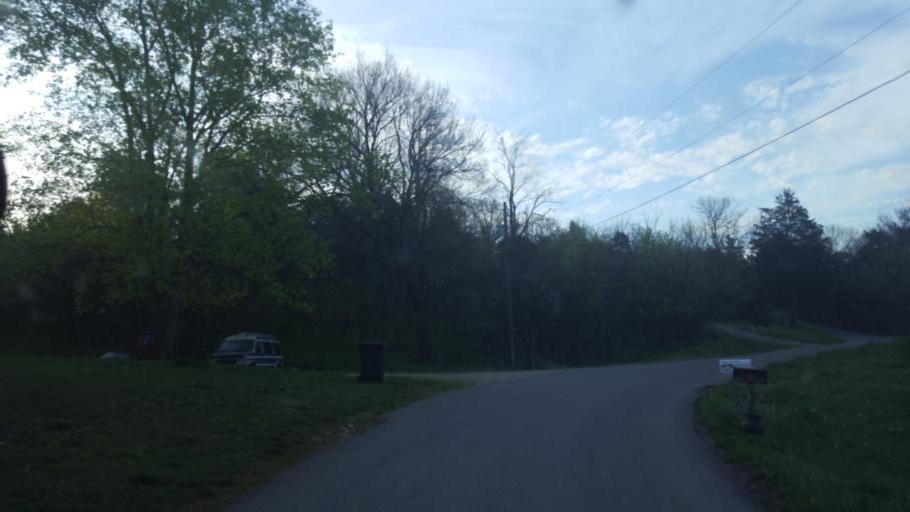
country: US
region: Kentucky
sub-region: Hart County
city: Horse Cave
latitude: 37.2220
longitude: -85.9621
